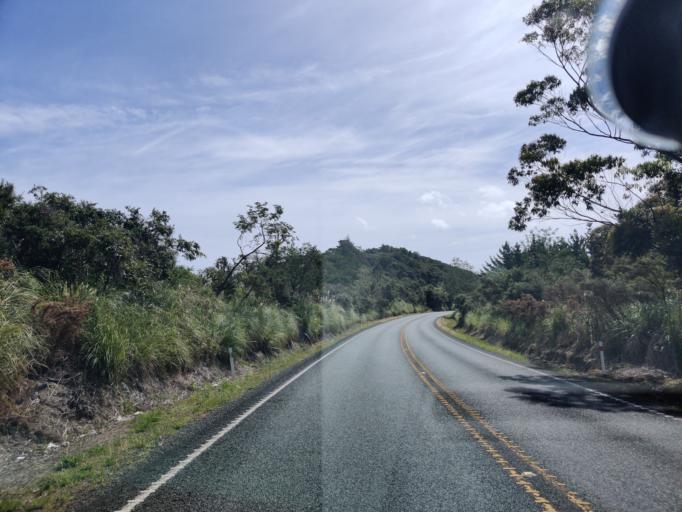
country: NZ
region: Northland
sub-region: Far North District
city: Kaitaia
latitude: -35.4866
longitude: 173.4406
